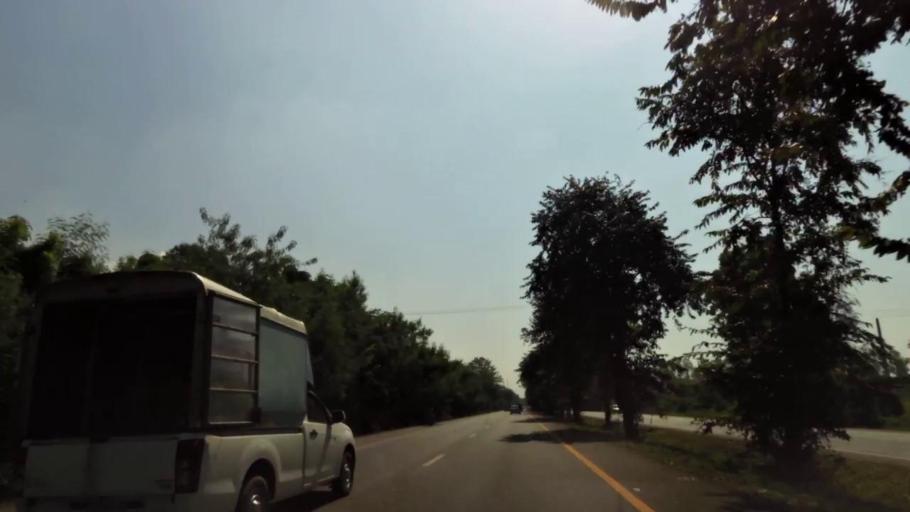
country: TH
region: Phichit
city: Bueng Na Rang
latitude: 16.1055
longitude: 100.1258
